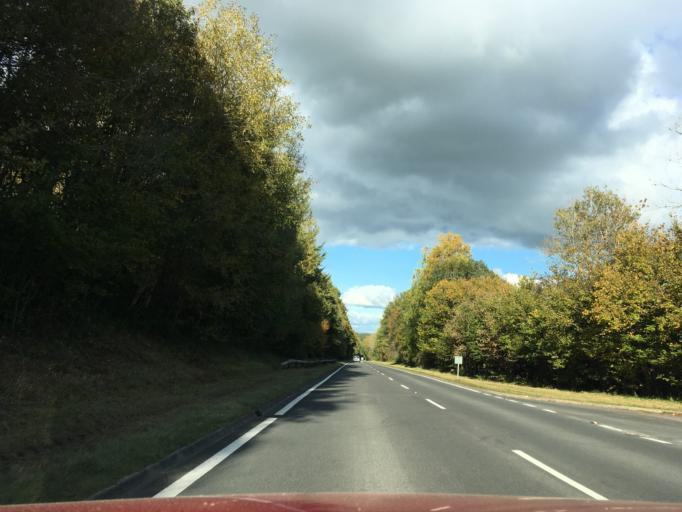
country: GB
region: Wales
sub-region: Sir Powys
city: Brecon
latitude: 51.8973
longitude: -3.4924
